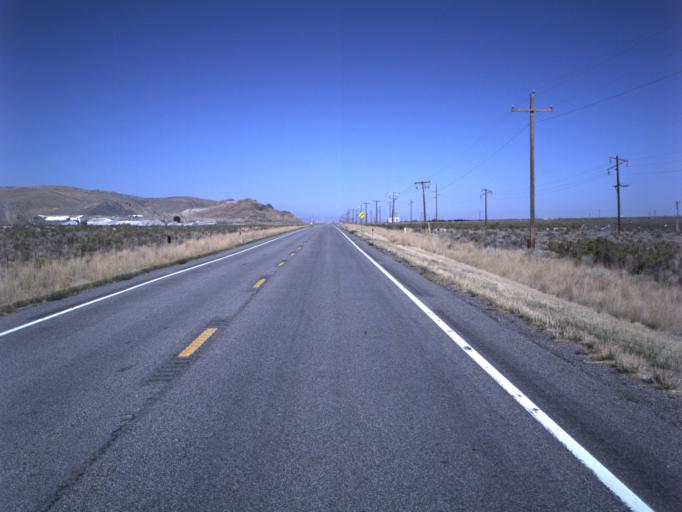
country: US
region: Utah
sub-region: Tooele County
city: Grantsville
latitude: 40.6701
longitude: -112.5464
